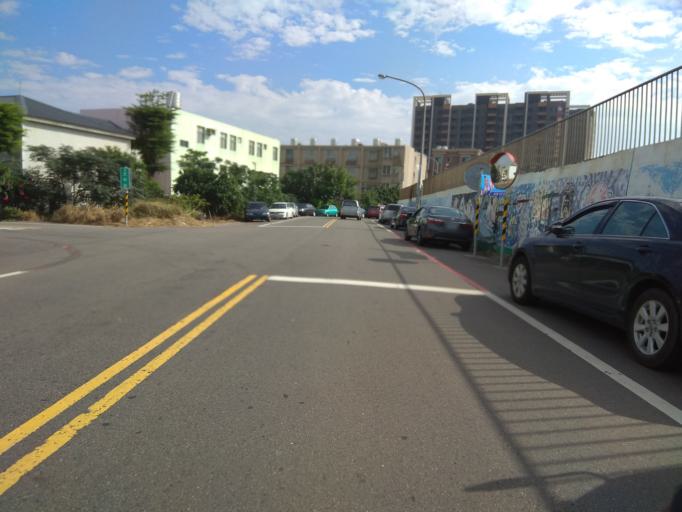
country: TW
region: Taiwan
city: Taoyuan City
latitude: 25.0639
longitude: 121.1926
